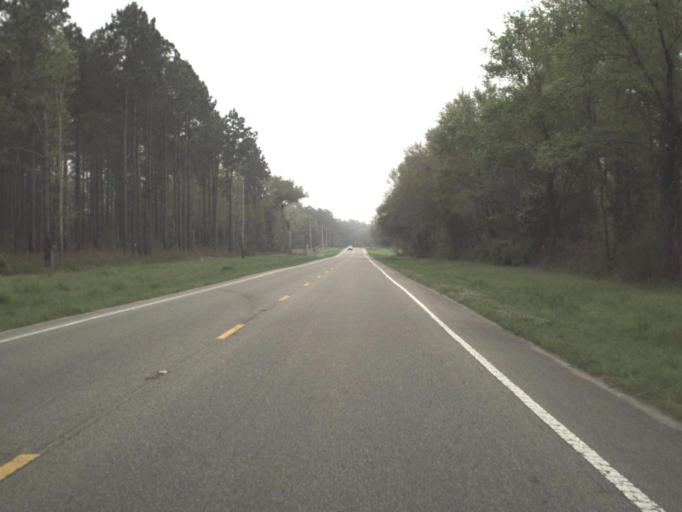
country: US
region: Florida
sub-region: Gadsden County
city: Gretna
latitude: 30.5534
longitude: -84.6769
